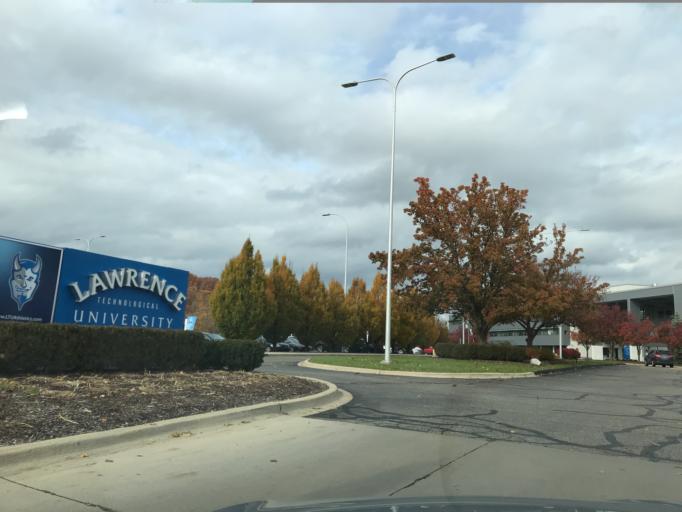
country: US
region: Michigan
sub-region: Oakland County
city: Southfield
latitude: 42.4728
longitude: -83.2496
